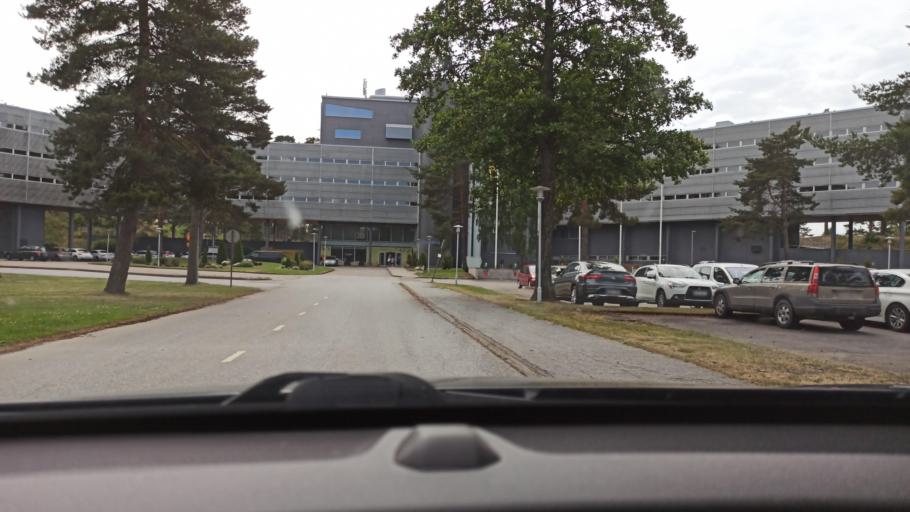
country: FI
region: Satakunta
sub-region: Pori
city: Luvia
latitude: 61.5709
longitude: 21.5192
